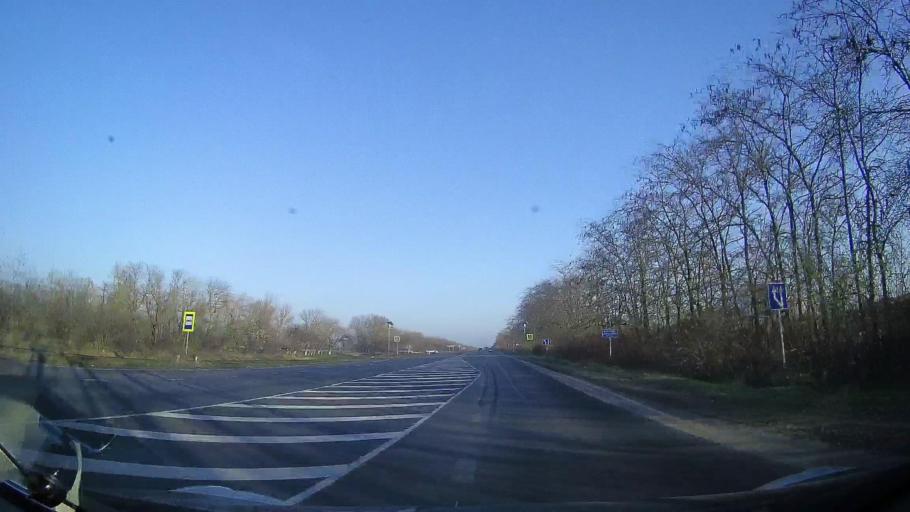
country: RU
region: Rostov
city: Kirovskaya
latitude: 47.0019
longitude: 39.9763
